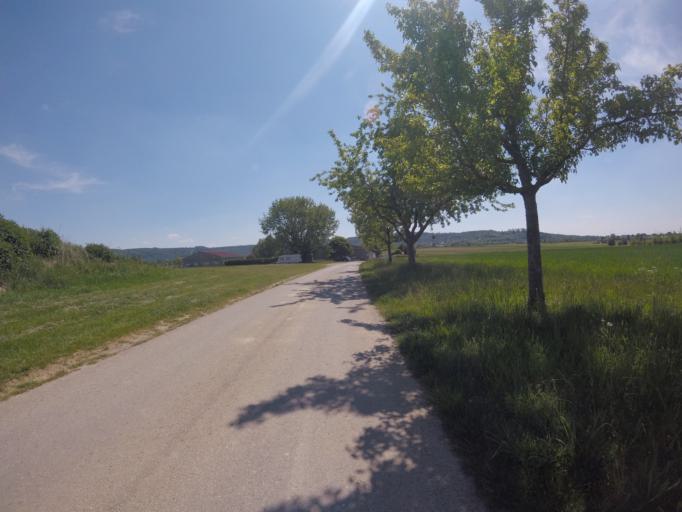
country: DE
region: Baden-Wuerttemberg
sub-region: Regierungsbezirk Stuttgart
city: Allmersbach im Tal
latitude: 48.9218
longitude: 9.4565
